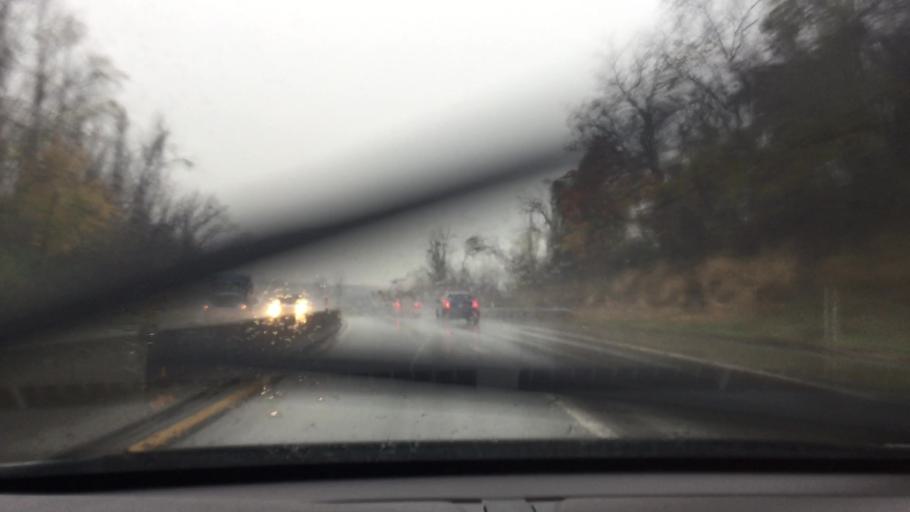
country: US
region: Pennsylvania
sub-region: Washington County
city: Ellsworth
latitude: 40.1682
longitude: -80.1054
